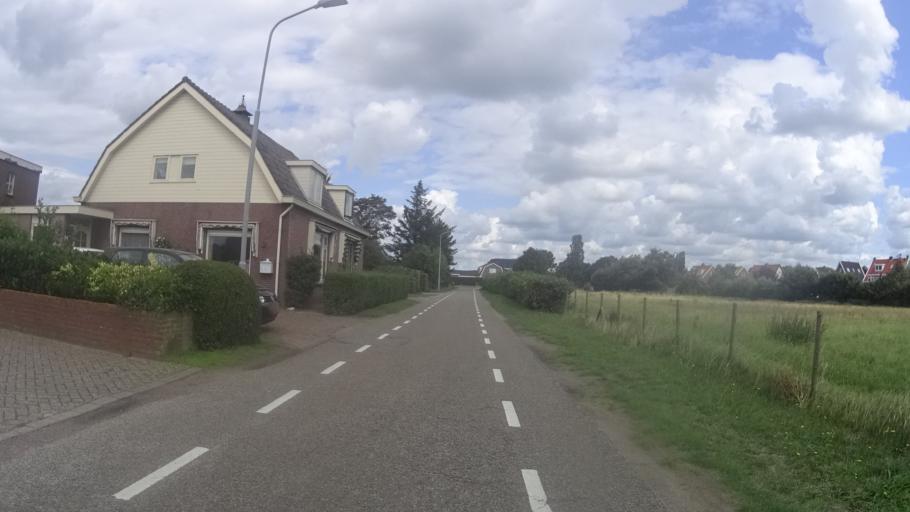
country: NL
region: North Holland
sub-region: Gemeente Heemskerk
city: Heemskerk
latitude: 52.5101
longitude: 4.6516
